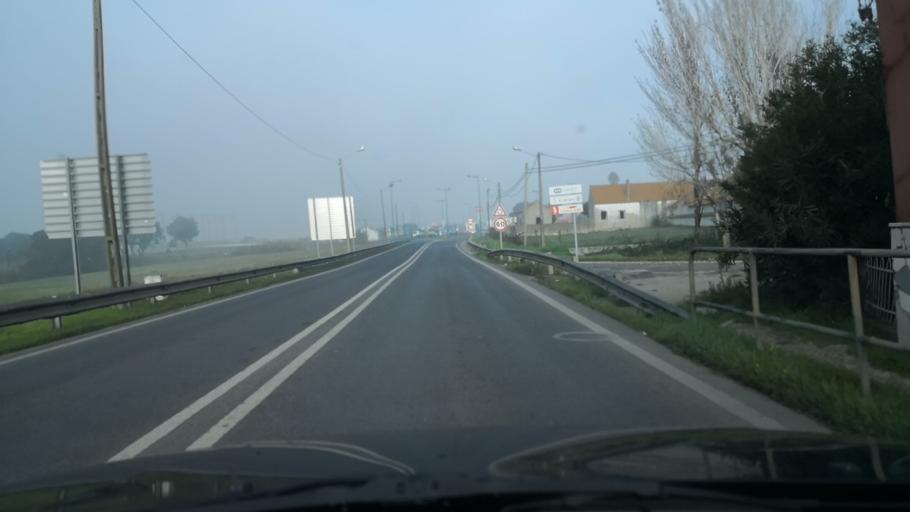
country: PT
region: Setubal
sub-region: Montijo
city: Montijo
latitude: 38.6848
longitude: -8.9429
